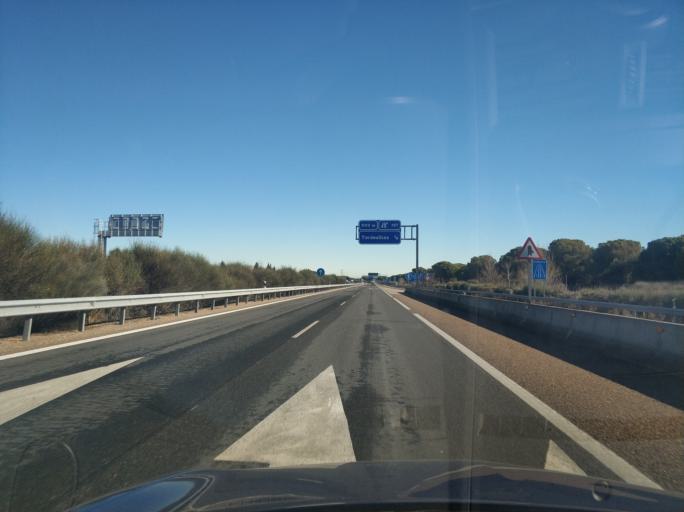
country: ES
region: Castille and Leon
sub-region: Provincia de Valladolid
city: Tordesillas
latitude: 41.4848
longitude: -5.0340
